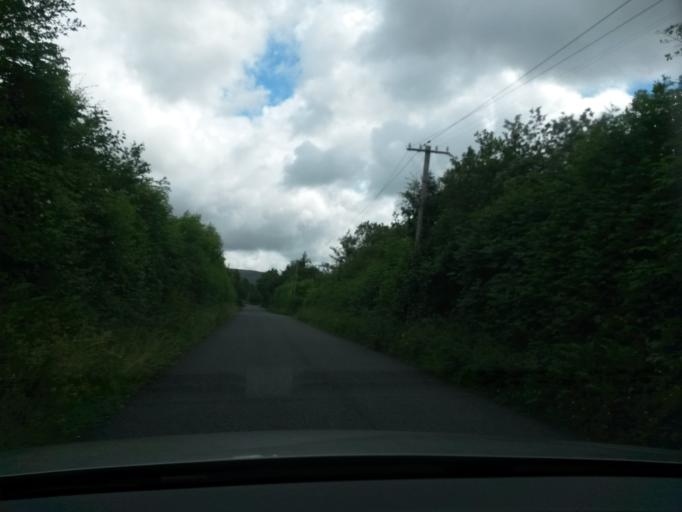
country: IE
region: Connaught
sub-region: Sligo
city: Sligo
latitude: 54.3307
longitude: -8.4364
